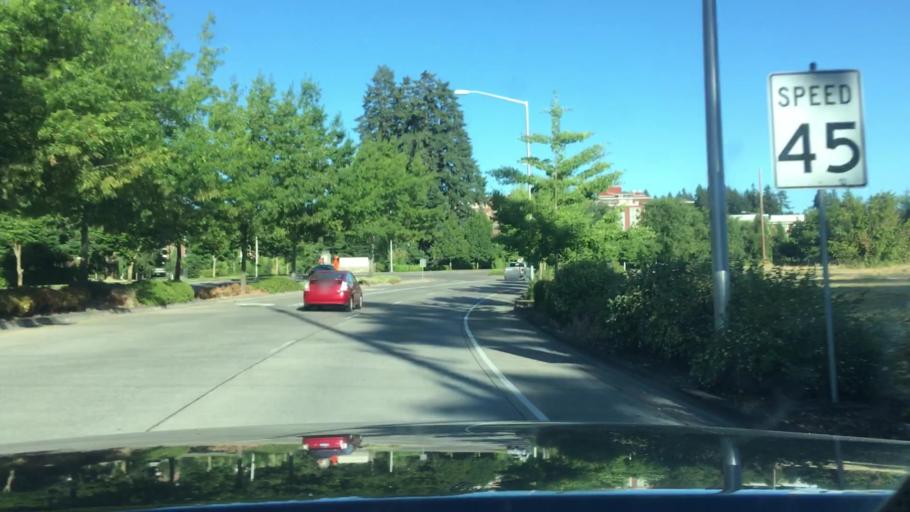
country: US
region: Oregon
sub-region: Lane County
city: Springfield
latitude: 44.0839
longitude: -123.0325
